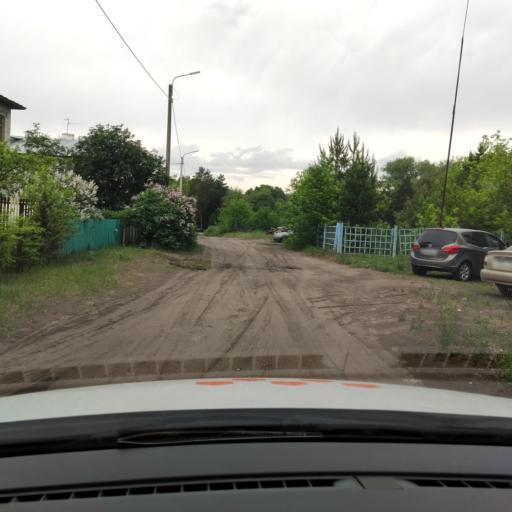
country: RU
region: Tatarstan
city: Staroye Arakchino
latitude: 55.8071
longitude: 48.9625
